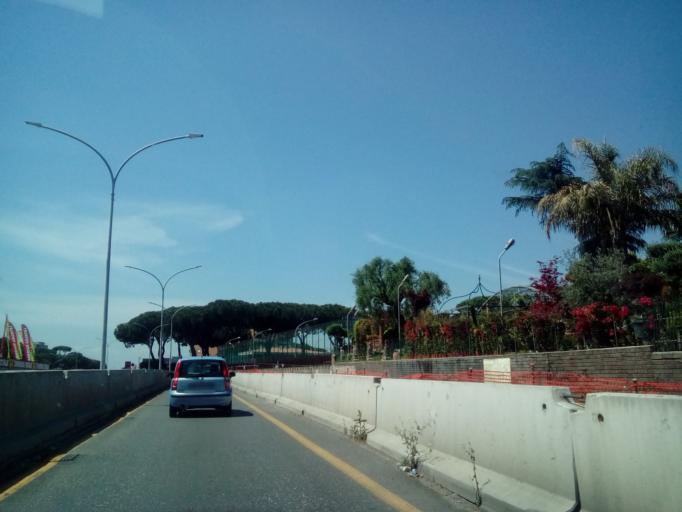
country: IT
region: Latium
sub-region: Citta metropolitana di Roma Capitale
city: Colle Verde
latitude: 41.9311
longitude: 12.5783
